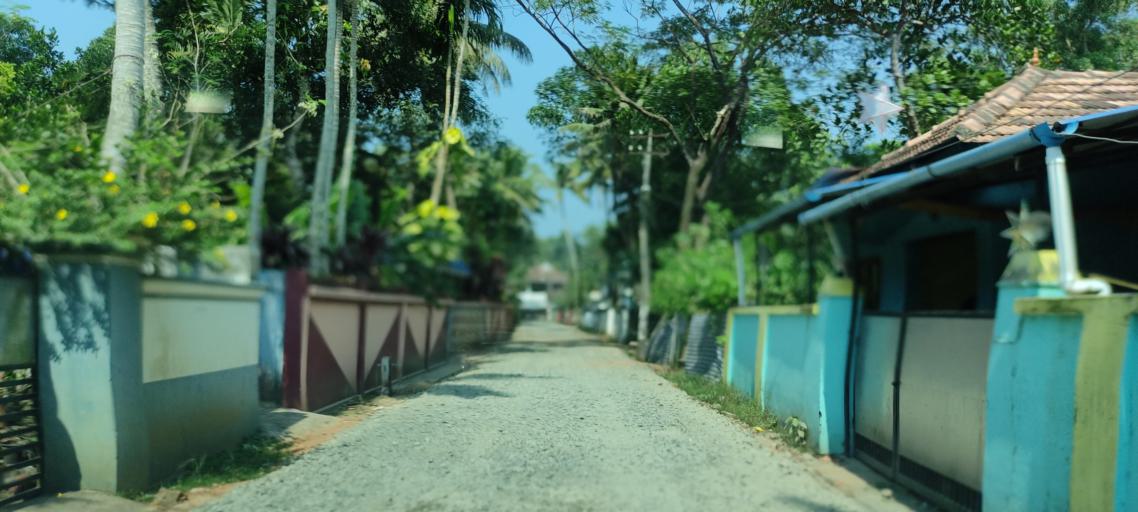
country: IN
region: Kerala
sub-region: Alappuzha
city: Alleppey
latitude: 9.5339
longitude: 76.3199
